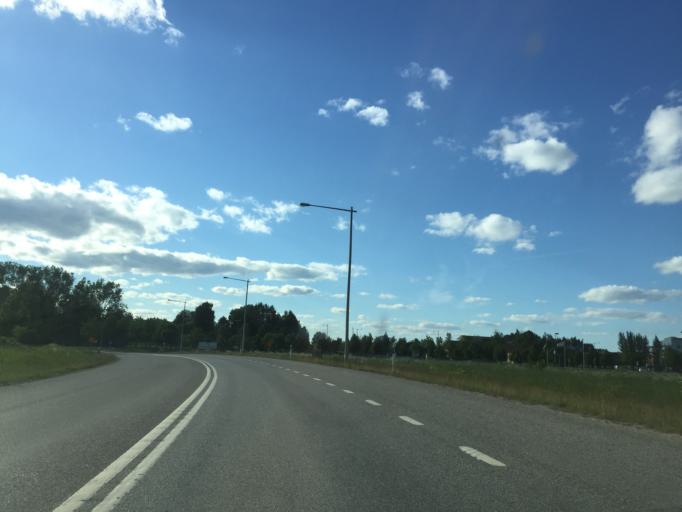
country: SE
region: OErebro
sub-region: Orebro Kommun
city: Orebro
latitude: 59.2517
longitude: 15.2384
